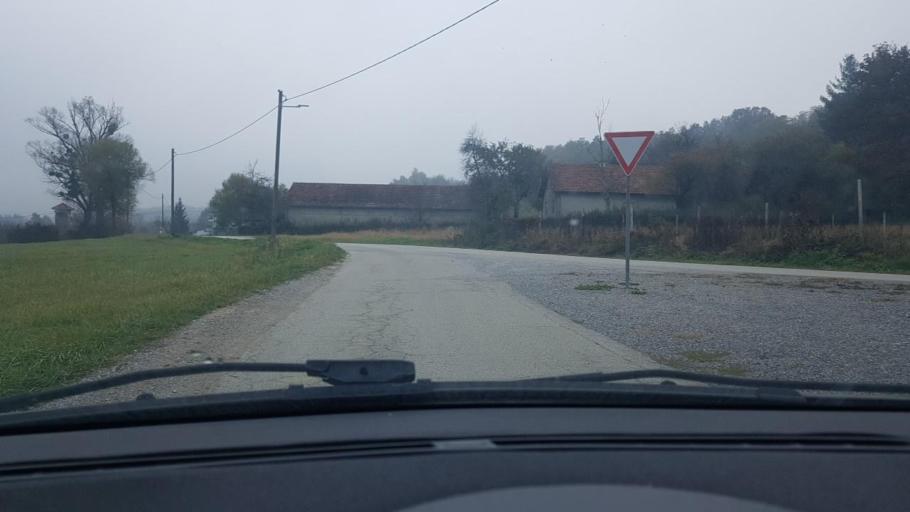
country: HR
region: Krapinsko-Zagorska
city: Zlatar
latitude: 46.0975
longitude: 16.1742
